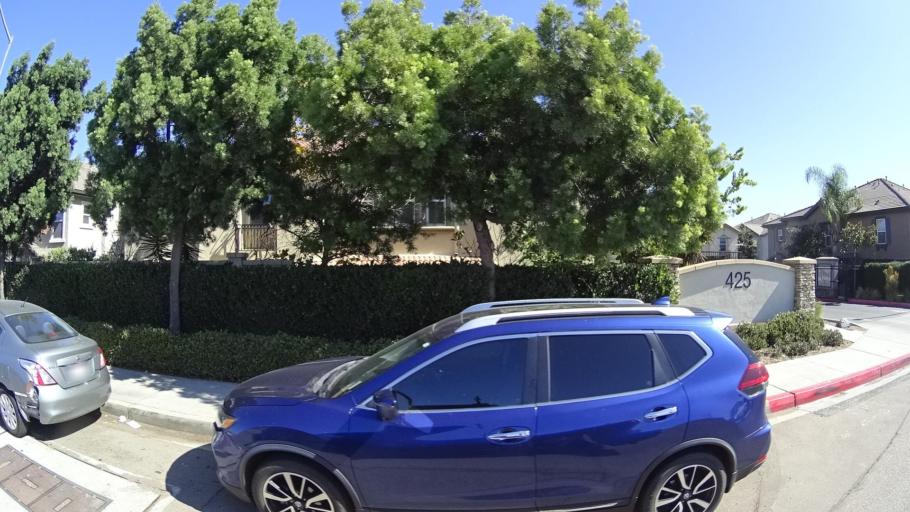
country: US
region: California
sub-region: San Diego County
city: La Presa
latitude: 32.6989
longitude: -117.0269
